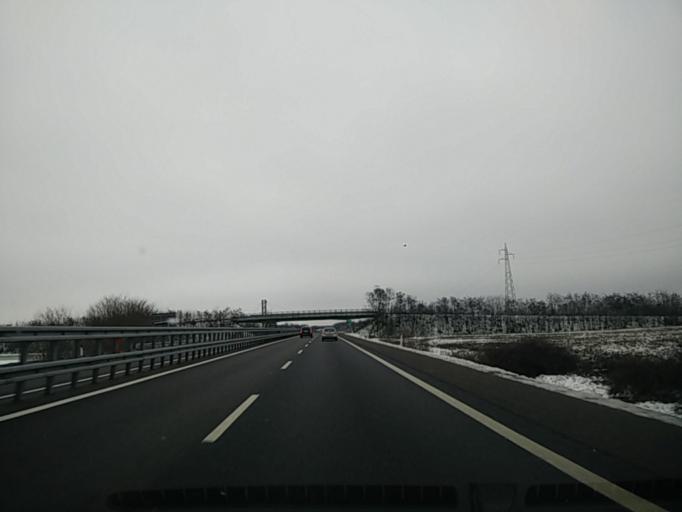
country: IT
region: Lombardy
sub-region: Provincia di Pavia
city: Robecco Pavese
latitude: 45.0416
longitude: 9.1472
